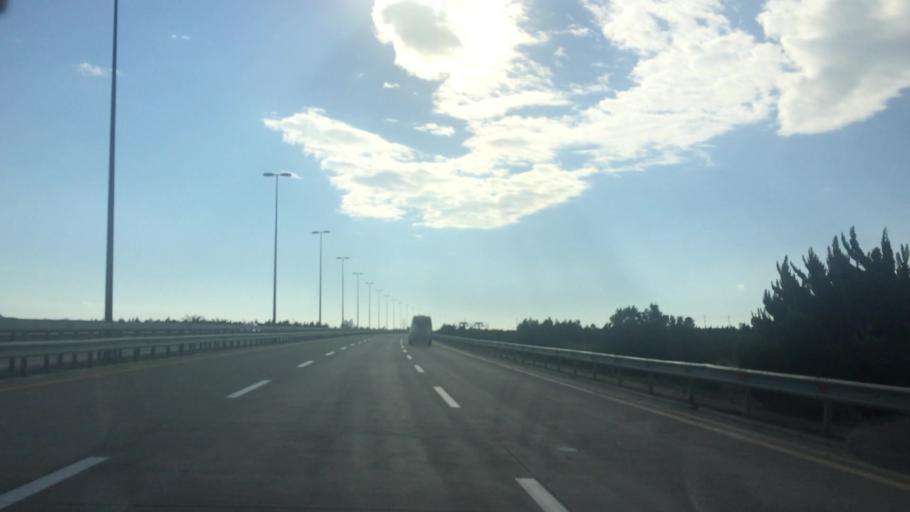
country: AZ
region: Baki
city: Hovsan
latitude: 40.3806
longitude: 50.0579
